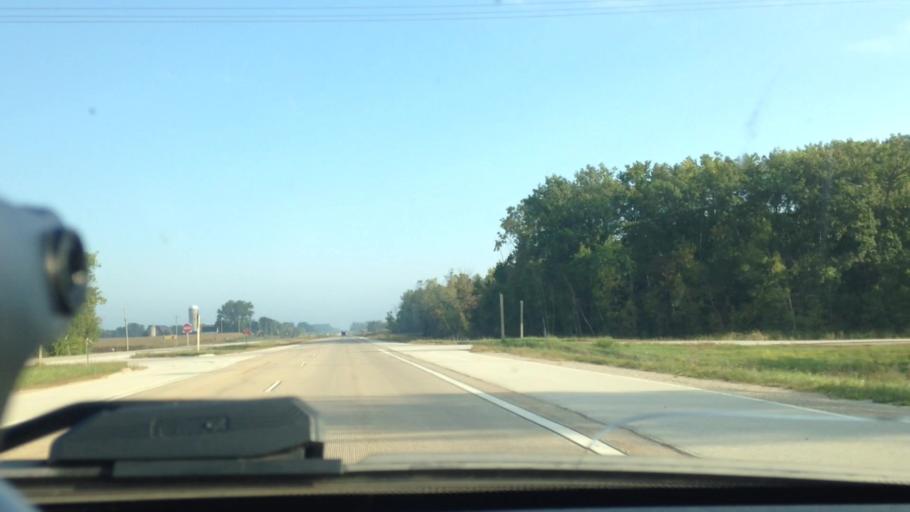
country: US
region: Wisconsin
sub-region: Oconto County
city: Oconto Falls
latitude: 45.0008
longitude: -88.0448
